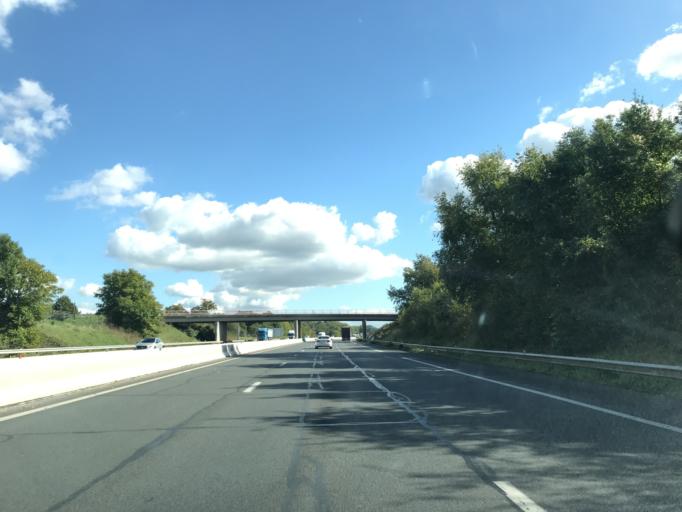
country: FR
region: Ile-de-France
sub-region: Departement de Seine-et-Marne
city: Nemours
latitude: 48.2850
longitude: 2.6958
